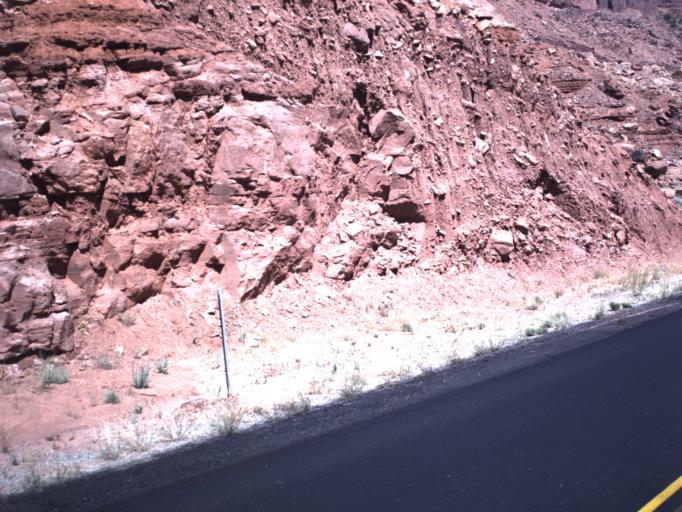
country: US
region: Utah
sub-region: Grand County
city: Moab
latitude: 38.6459
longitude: -109.4956
